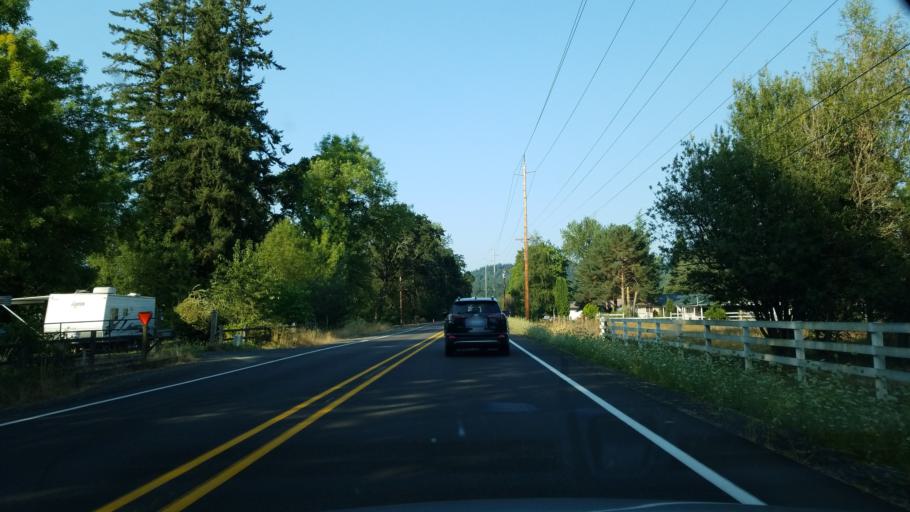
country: US
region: Oregon
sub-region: Clackamas County
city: Molalla
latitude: 45.1645
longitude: -122.5284
